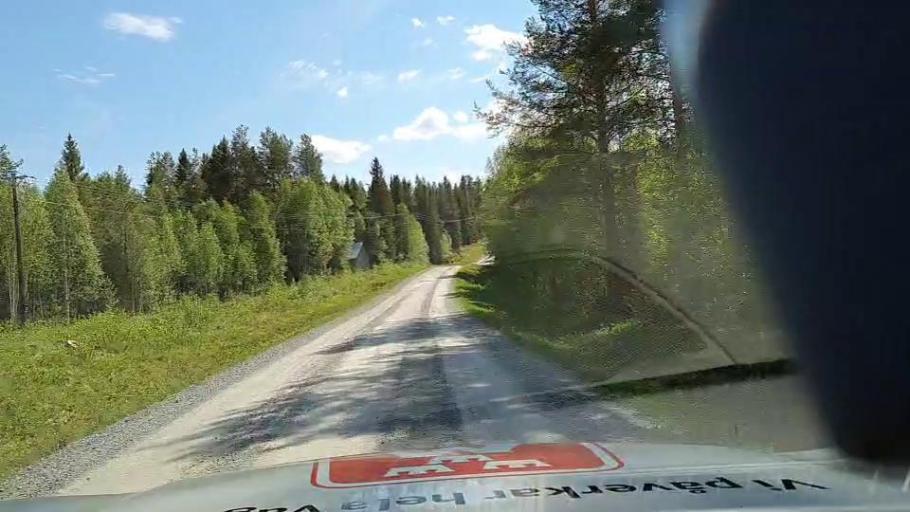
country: SE
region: Jaemtland
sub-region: Stroemsunds Kommun
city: Stroemsund
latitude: 64.4671
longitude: 15.5948
